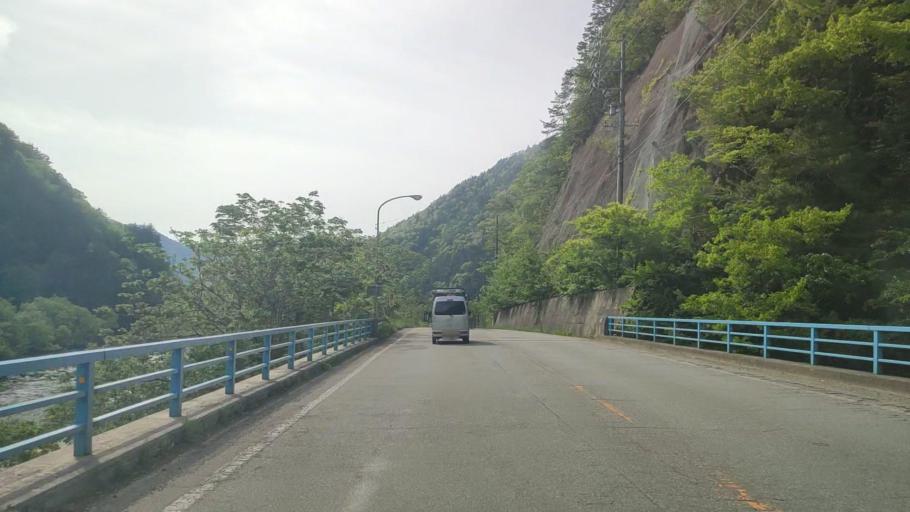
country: JP
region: Gifu
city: Takayama
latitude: 36.2664
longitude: 137.4258
